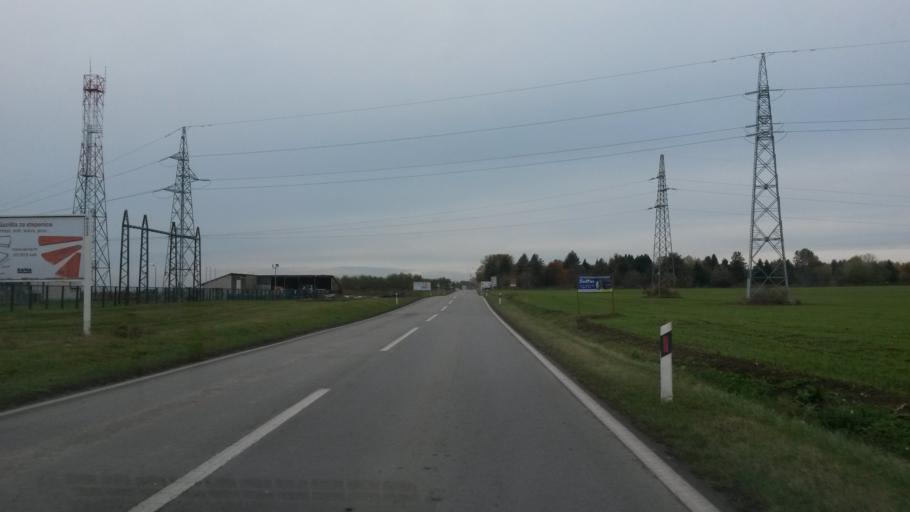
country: HR
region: Osjecko-Baranjska
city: Beli Manastir
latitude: 45.7587
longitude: 18.6294
